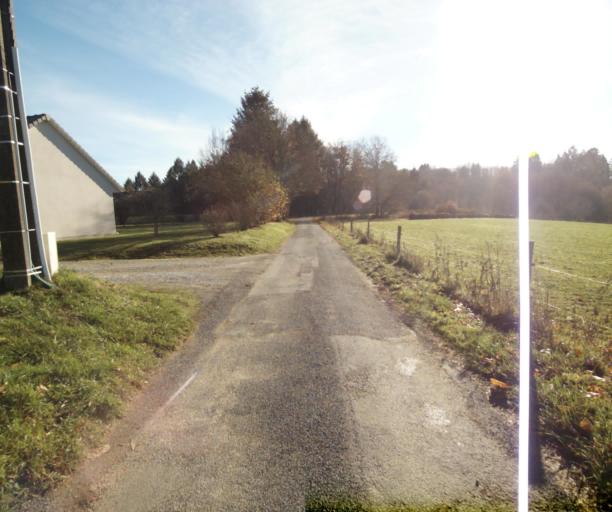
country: FR
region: Limousin
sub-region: Departement de la Correze
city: Laguenne
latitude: 45.2375
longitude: 1.7571
